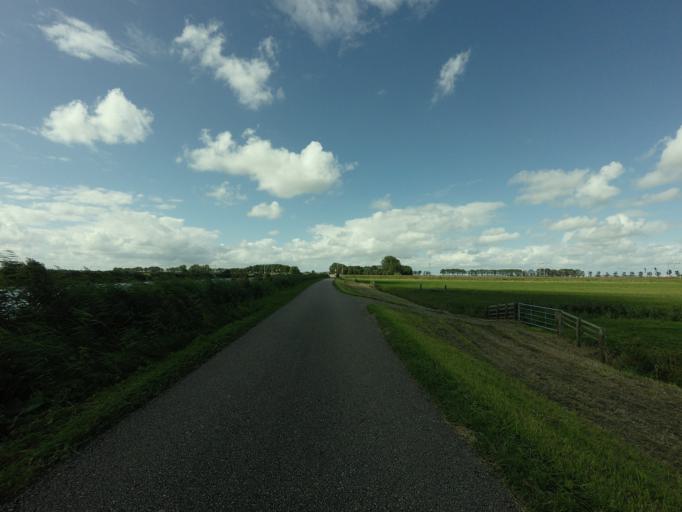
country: NL
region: North Holland
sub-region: Gemeente Hoorn
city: Hoorn
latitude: 52.5939
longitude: 5.0092
